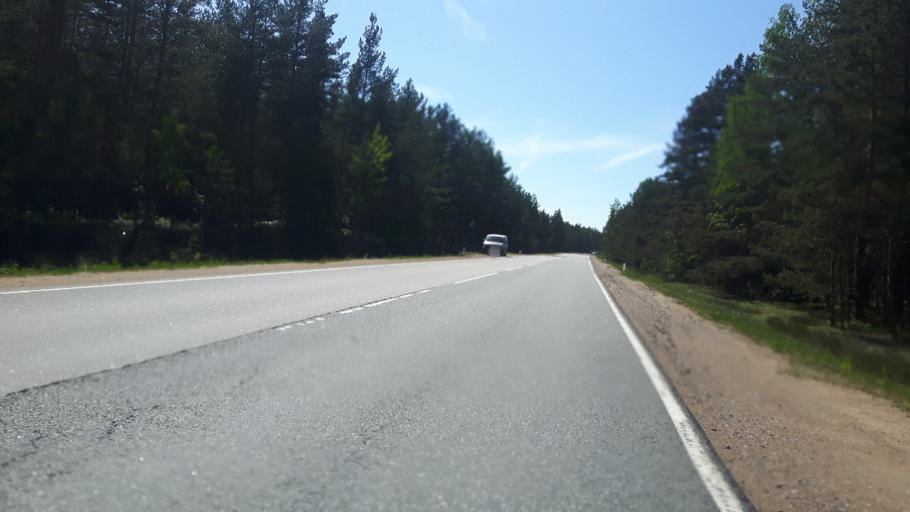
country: RU
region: Leningrad
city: Sista-Palkino
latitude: 59.7672
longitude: 28.7510
